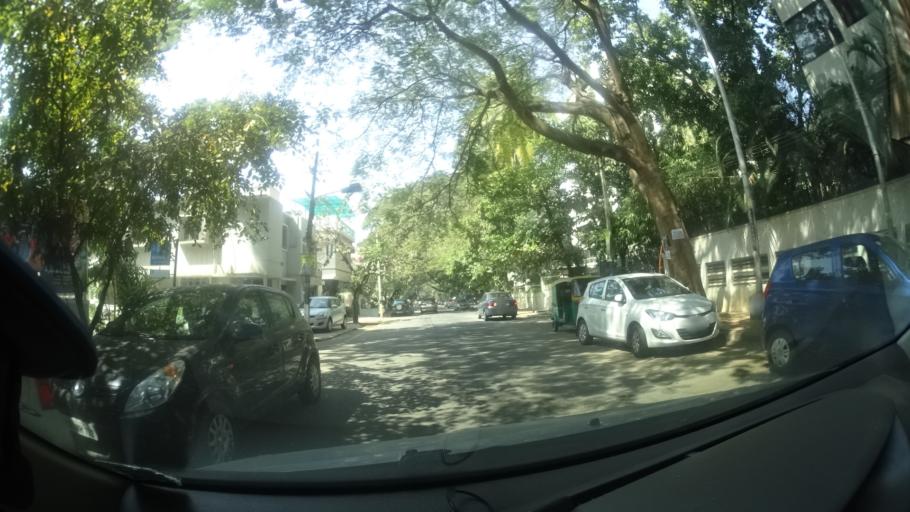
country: IN
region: Karnataka
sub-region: Bangalore Urban
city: Bangalore
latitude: 13.0095
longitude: 77.5785
